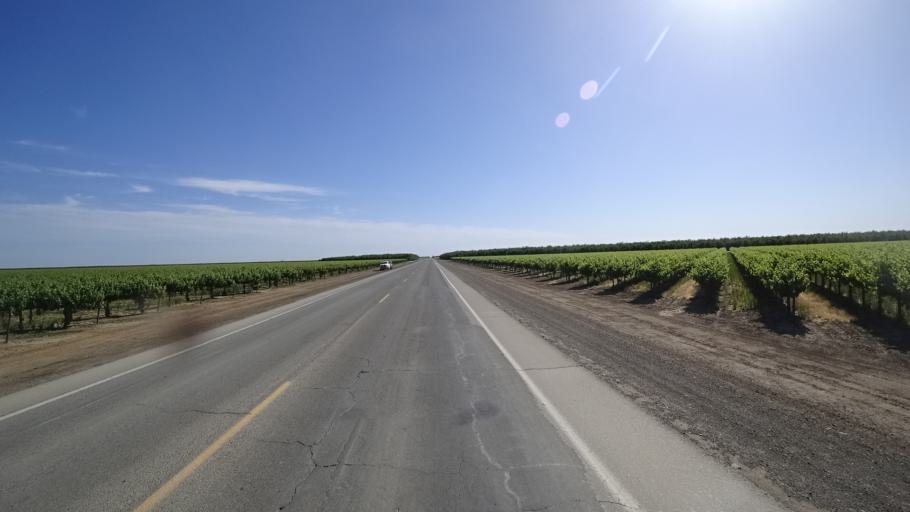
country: US
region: California
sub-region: Fresno County
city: Huron
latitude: 36.1419
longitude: -120.0061
